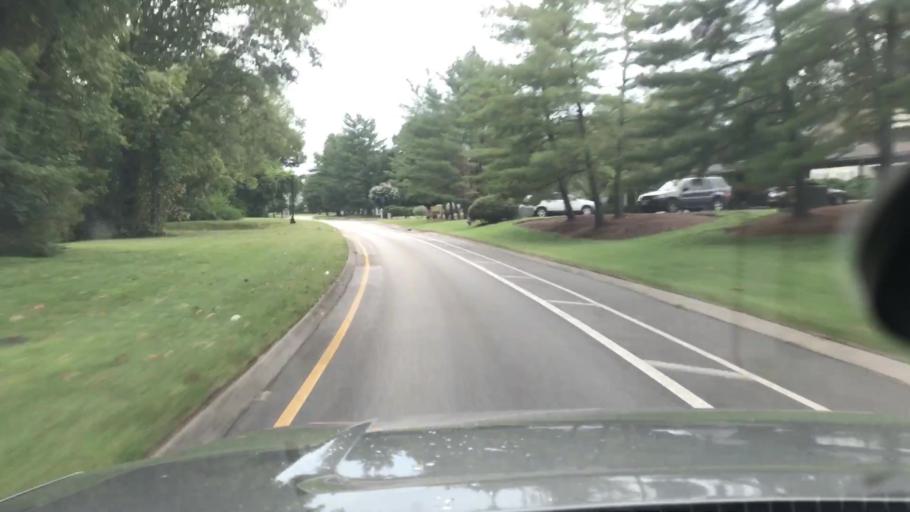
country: US
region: Tennessee
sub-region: Rutherford County
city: La Vergne
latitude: 36.0897
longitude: -86.6378
